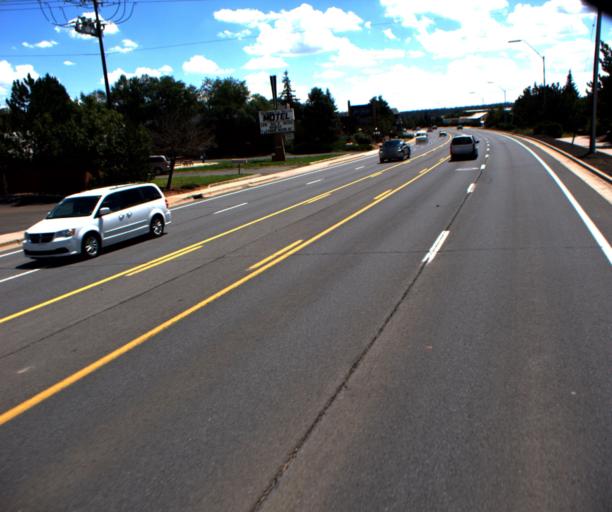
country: US
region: Arizona
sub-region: Coconino County
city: Flagstaff
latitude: 35.1942
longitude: -111.6388
